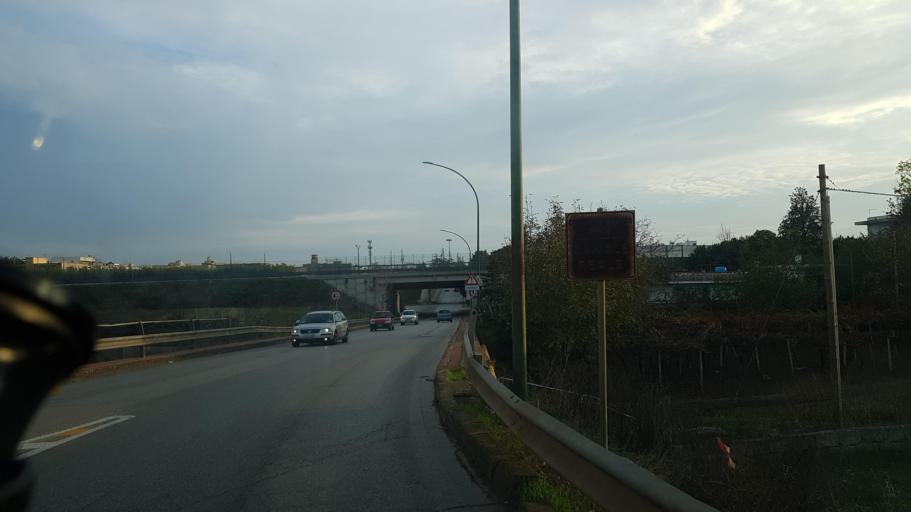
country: IT
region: Apulia
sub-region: Provincia di Brindisi
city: Latiano
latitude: 40.5596
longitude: 17.7150
